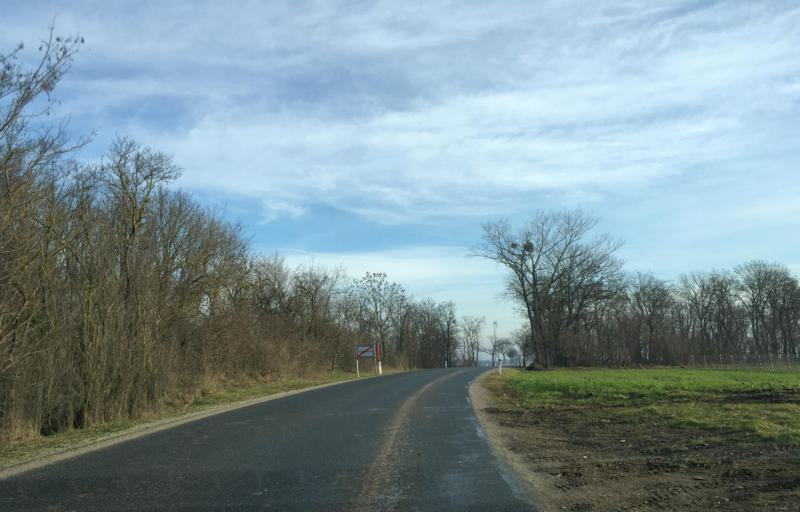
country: AT
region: Lower Austria
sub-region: Politischer Bezirk Ganserndorf
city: Andlersdorf
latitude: 48.1909
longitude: 16.6506
